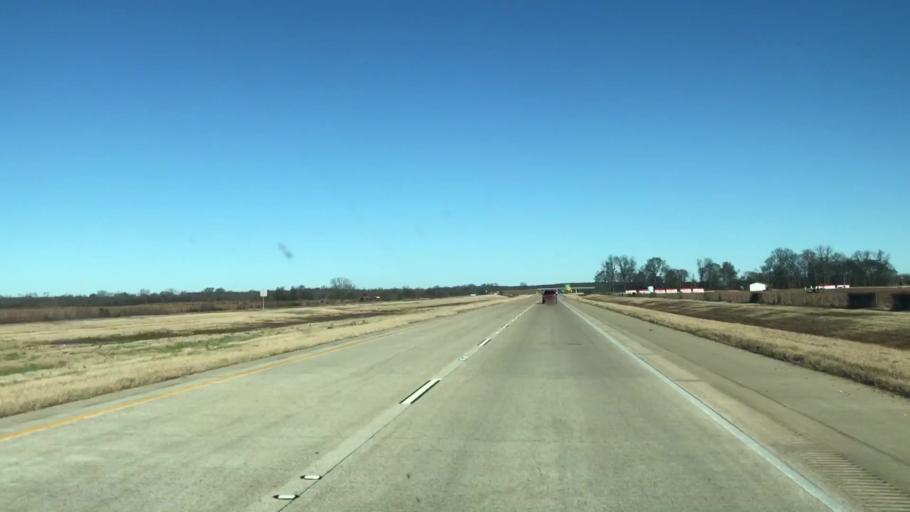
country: US
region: Louisiana
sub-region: Caddo Parish
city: Oil City
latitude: 32.7562
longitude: -93.8840
